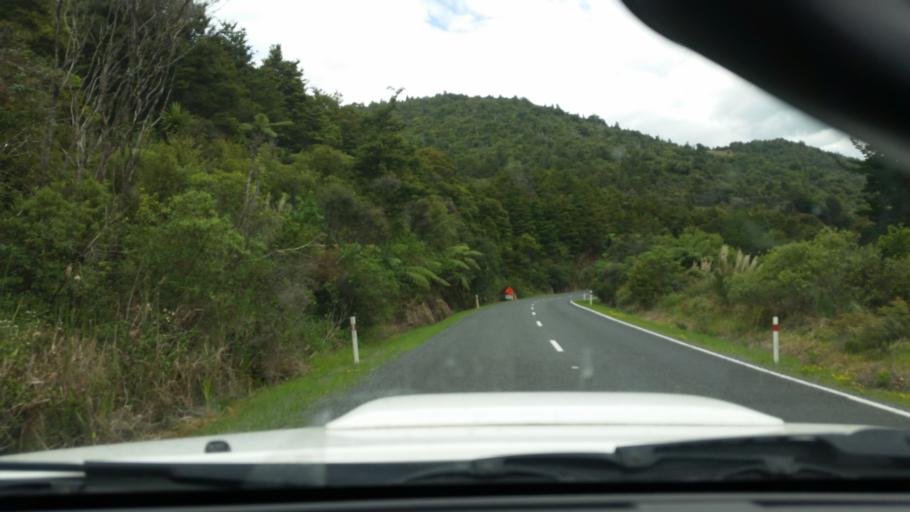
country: NZ
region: Northland
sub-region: Kaipara District
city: Dargaville
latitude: -35.7669
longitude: 173.9077
